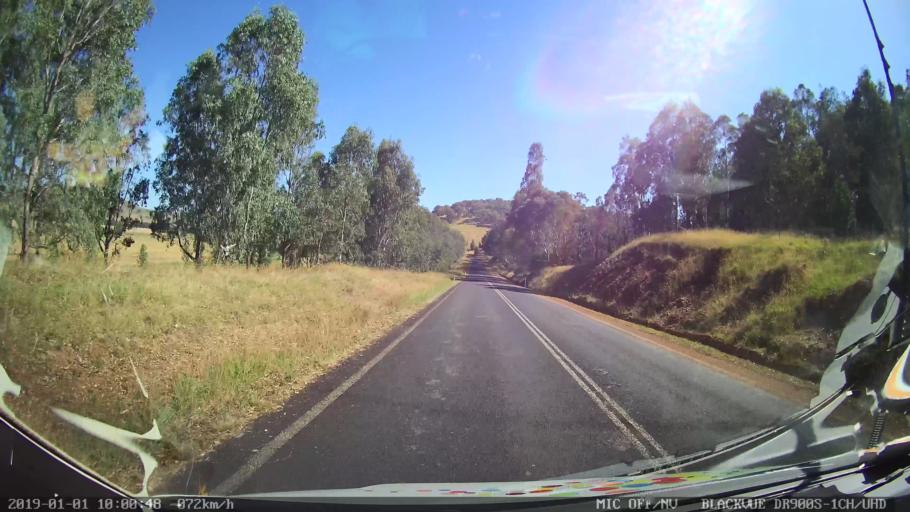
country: AU
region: New South Wales
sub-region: Snowy River
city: Jindabyne
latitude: -36.1983
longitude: 148.1026
